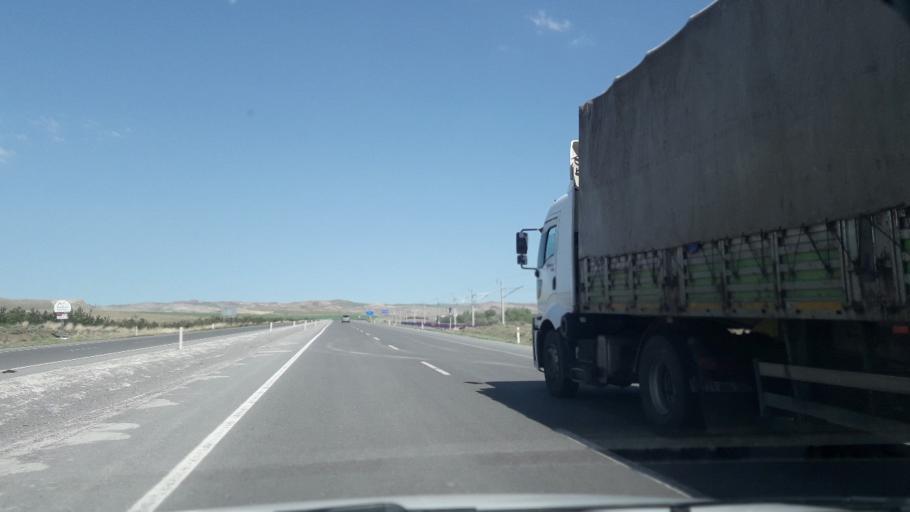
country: TR
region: Sivas
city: Ulas
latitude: 39.4512
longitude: 37.0254
